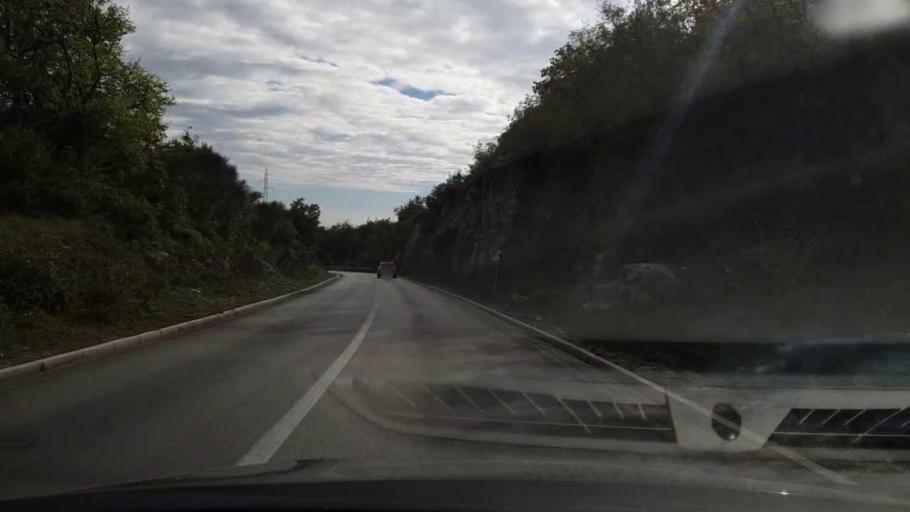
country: ME
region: Herceg Novi
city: Herceg-Novi
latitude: 42.4753
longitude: 18.5288
